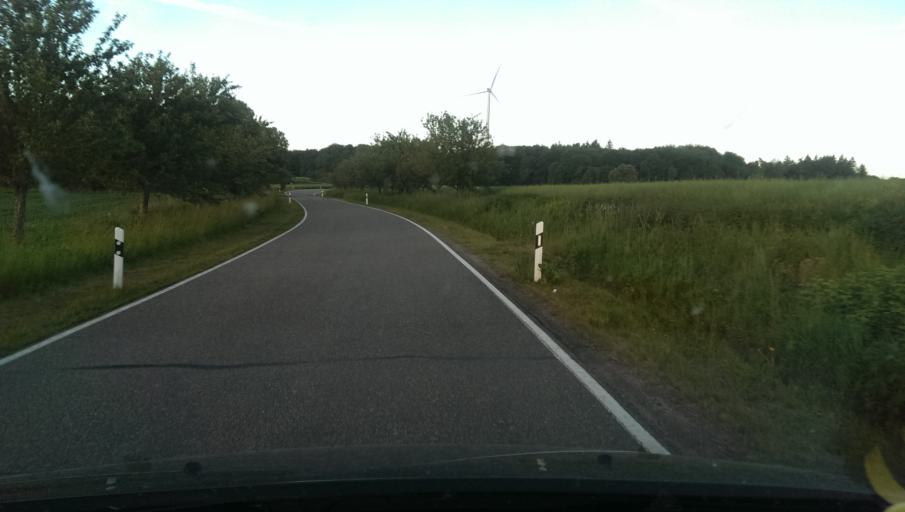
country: DE
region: Baden-Wuerttemberg
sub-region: Regierungsbezirk Stuttgart
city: Buch am Ahorn
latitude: 49.5404
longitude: 9.5656
